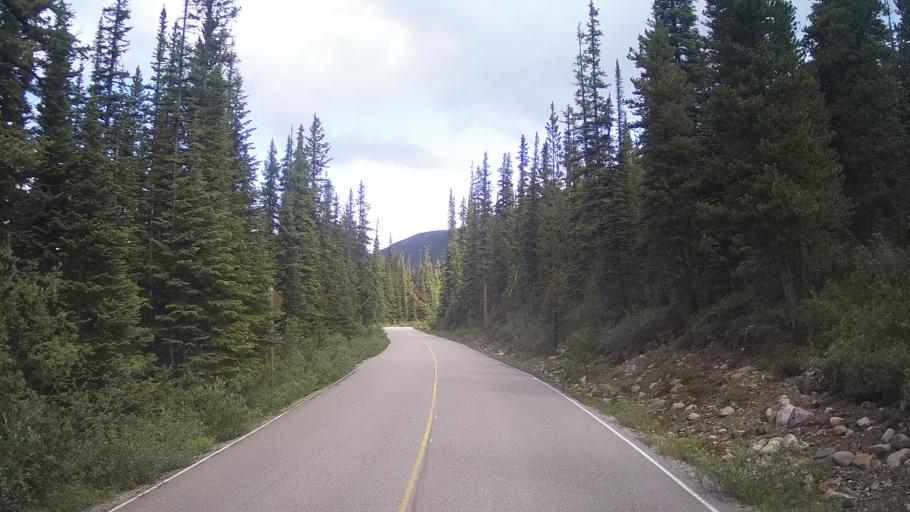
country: CA
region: Alberta
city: Jasper Park Lodge
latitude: 52.7154
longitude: -118.0551
